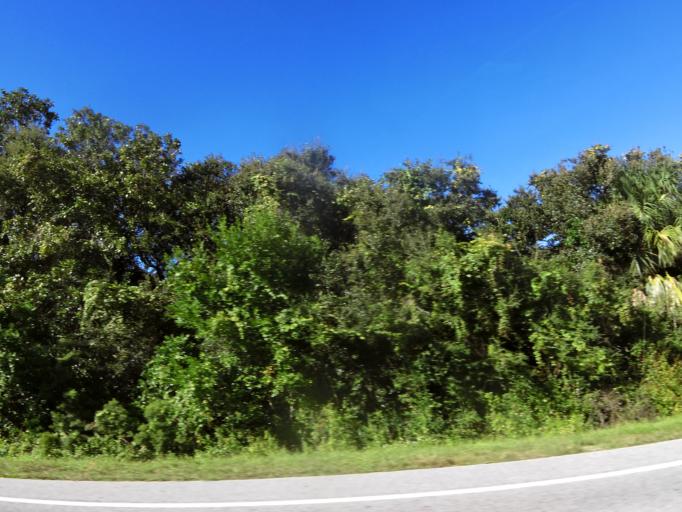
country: US
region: Florida
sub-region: Saint Johns County
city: Saint Augustine Beach
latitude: 29.8620
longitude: -81.2733
